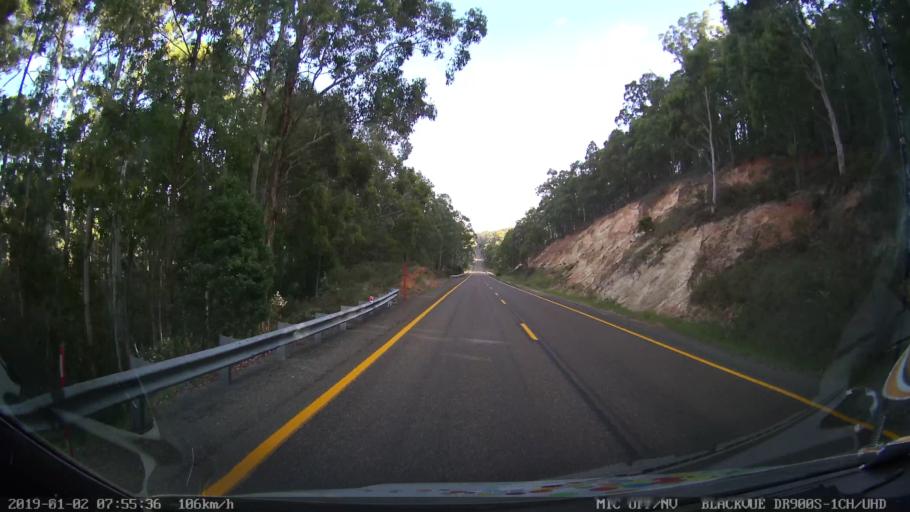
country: AU
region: New South Wales
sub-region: Tumut Shire
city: Tumut
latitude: -35.6824
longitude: 148.4866
